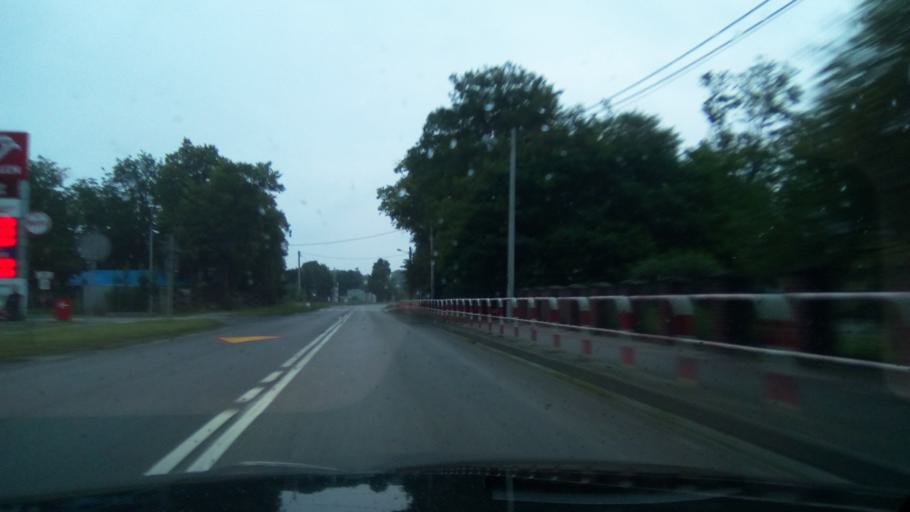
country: PL
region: Greater Poland Voivodeship
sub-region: Powiat poznanski
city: Kobylnica
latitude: 52.4485
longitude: 17.0829
